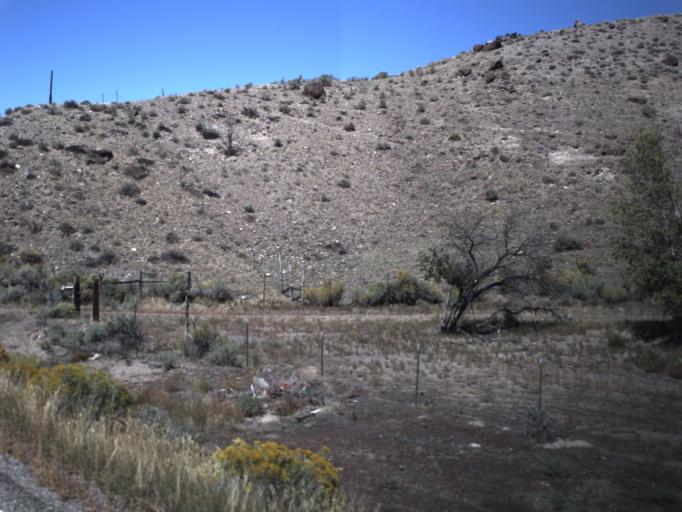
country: US
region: Utah
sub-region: Piute County
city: Junction
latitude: 38.1974
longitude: -112.1496
